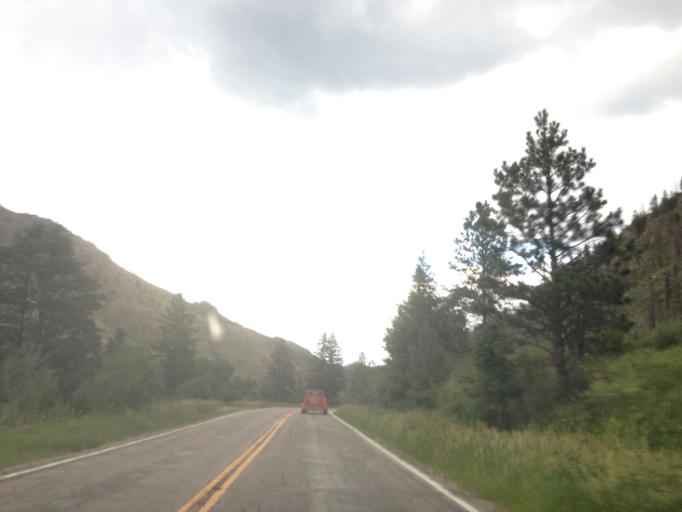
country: US
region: Colorado
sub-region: Larimer County
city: Laporte
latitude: 40.6823
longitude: -105.4034
